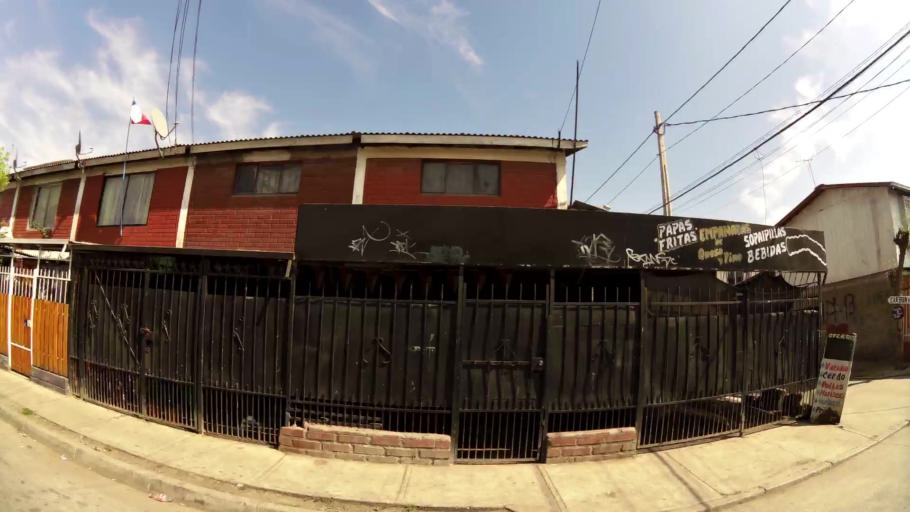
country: CL
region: Santiago Metropolitan
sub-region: Provincia de Santiago
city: La Pintana
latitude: -33.5621
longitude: -70.6408
